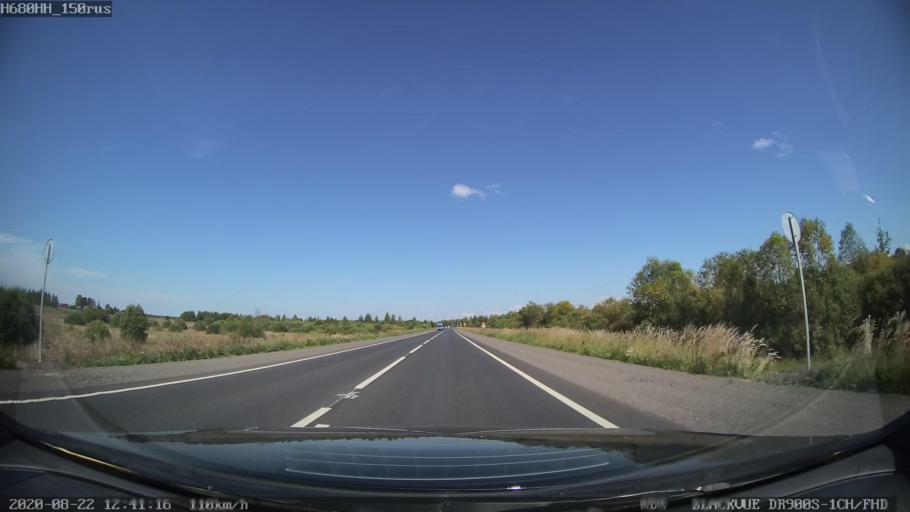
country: RU
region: Tverskaya
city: Rameshki
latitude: 57.3460
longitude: 36.0982
